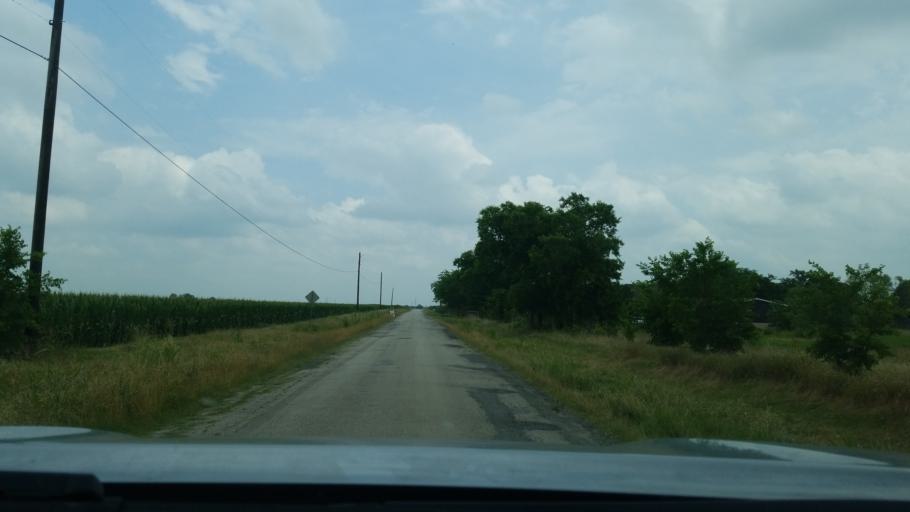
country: US
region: Texas
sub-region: Guadalupe County
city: Geronimo
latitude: 29.6802
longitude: -98.0110
